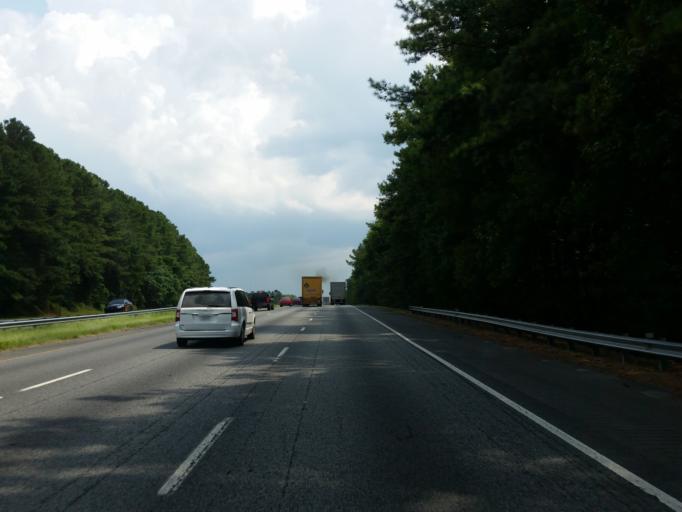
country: US
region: Georgia
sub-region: Monroe County
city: Forsyth
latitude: 33.0984
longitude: -83.9995
